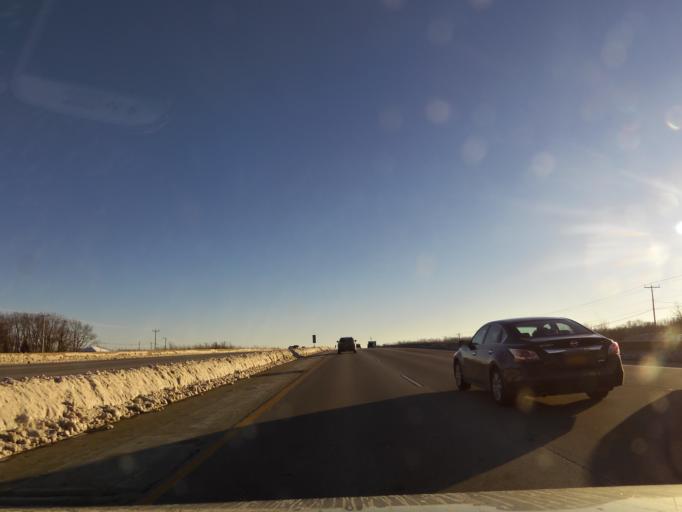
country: US
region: Wisconsin
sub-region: Racine County
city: Franksville
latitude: 42.7445
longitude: -87.9542
